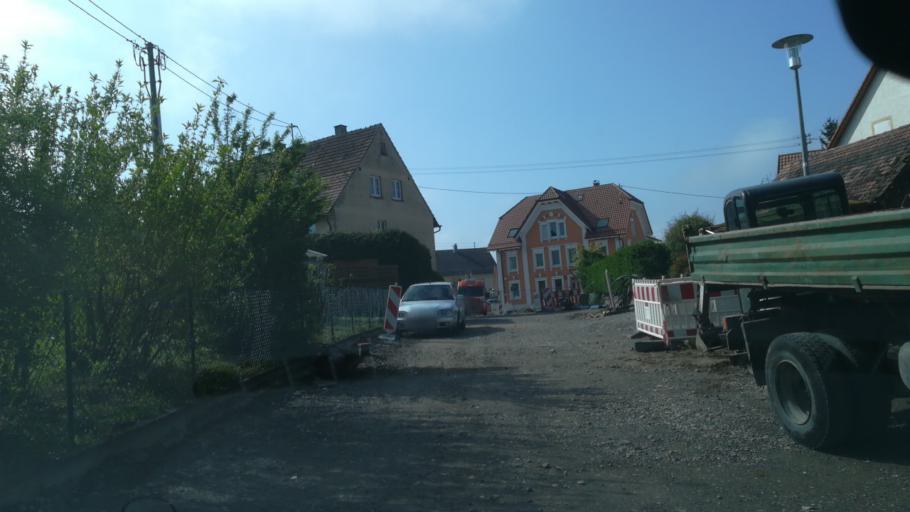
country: DE
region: Baden-Wuerttemberg
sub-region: Freiburg Region
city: Hilzingen
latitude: 47.7659
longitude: 8.7846
